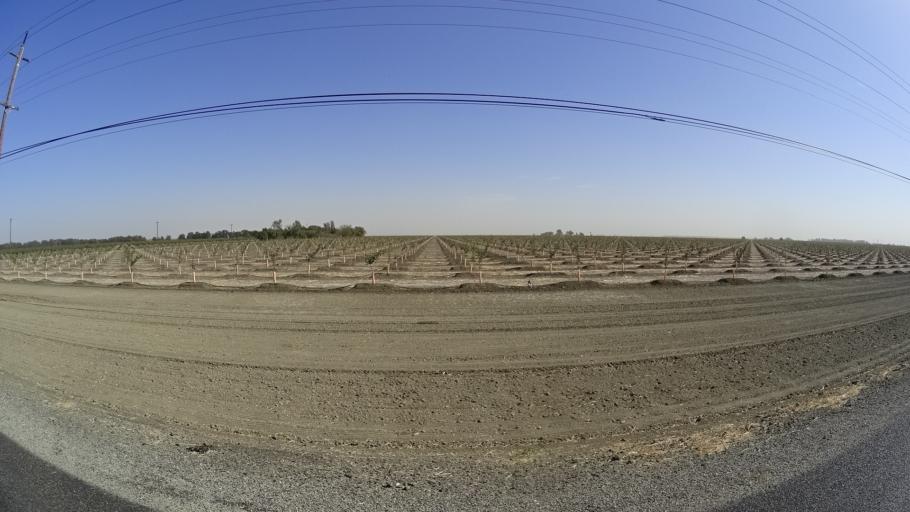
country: US
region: California
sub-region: Yolo County
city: Woodland
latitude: 38.6252
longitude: -121.7295
